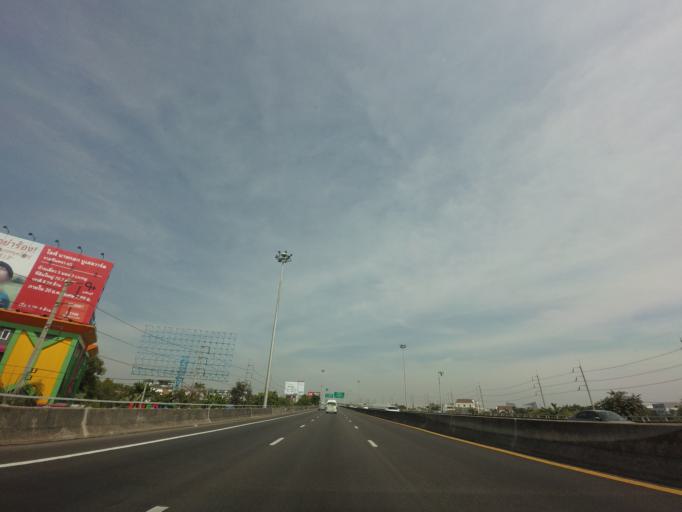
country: TH
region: Bangkok
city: Bang Khen
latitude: 13.8378
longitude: 100.6335
